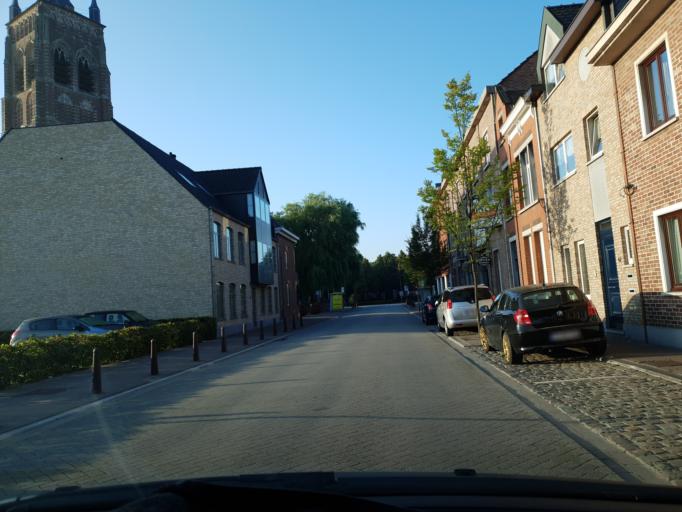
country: BE
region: Flanders
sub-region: Provincie Antwerpen
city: Brecht
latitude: 51.3476
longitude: 4.6786
